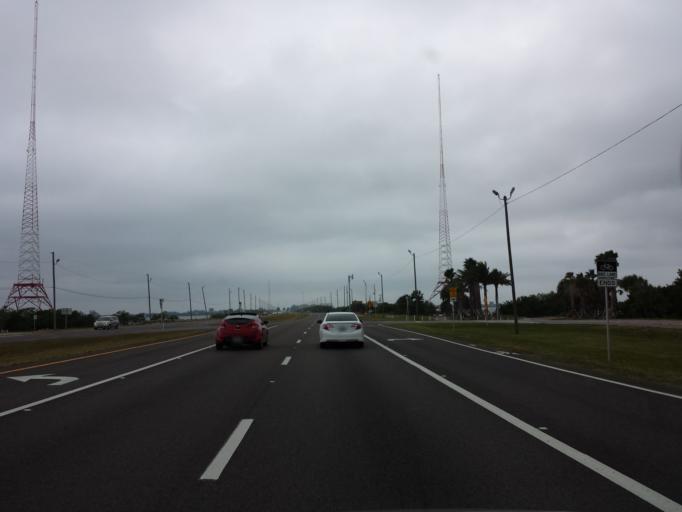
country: US
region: Florida
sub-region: Pinellas County
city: Gandy
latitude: 27.8780
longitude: -82.5877
